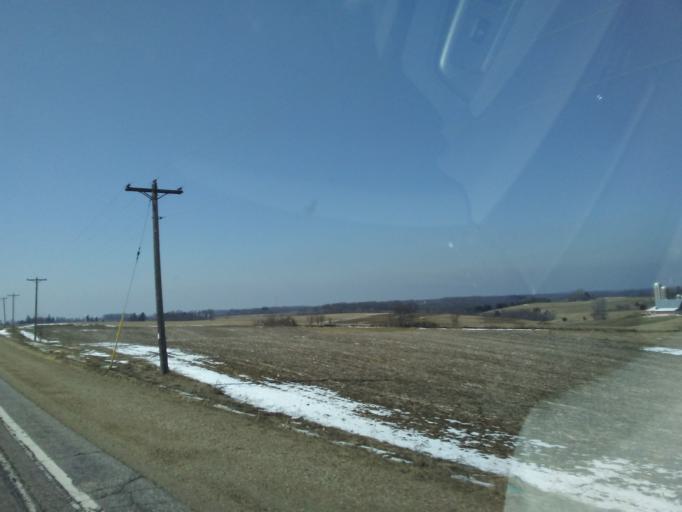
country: US
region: Wisconsin
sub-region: Vernon County
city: Westby
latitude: 43.6643
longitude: -90.8924
